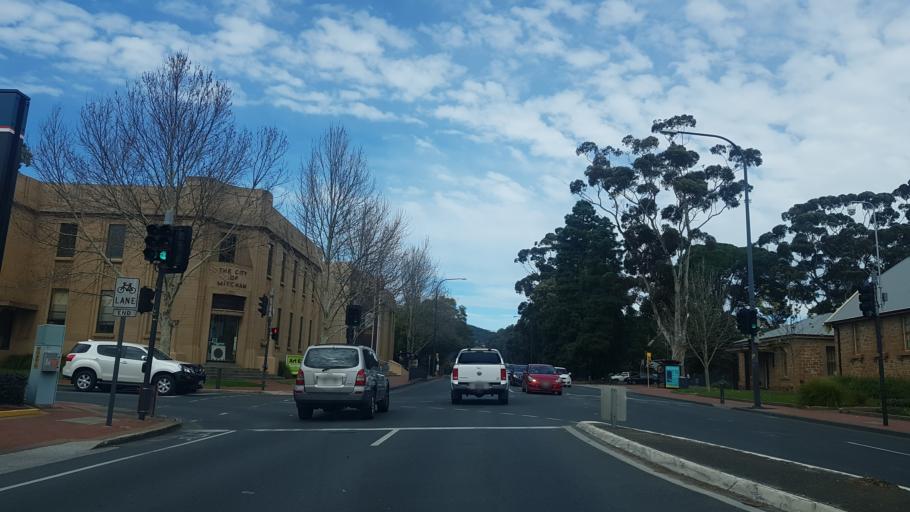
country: AU
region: South Australia
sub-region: Mitcham
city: Hawthorn
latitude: -34.9762
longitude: 138.6095
